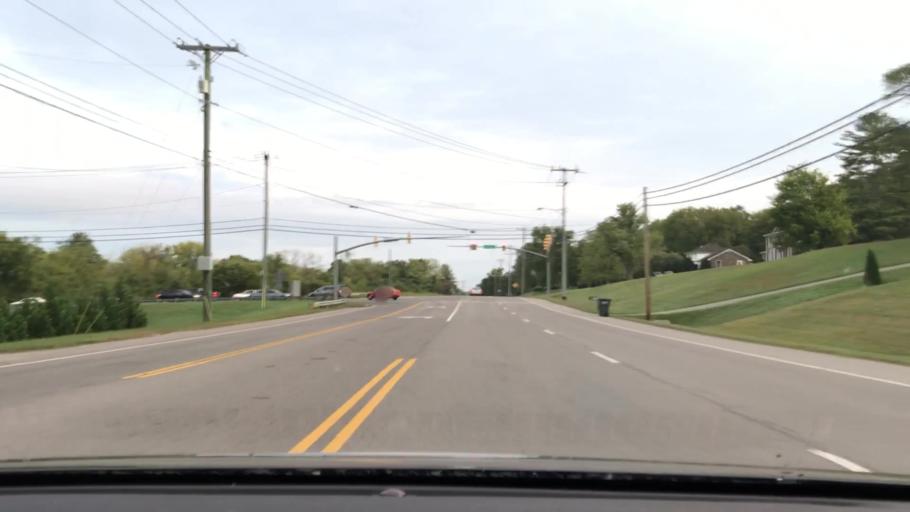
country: US
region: Tennessee
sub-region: Williamson County
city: Brentwood Estates
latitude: 36.0297
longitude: -86.7441
